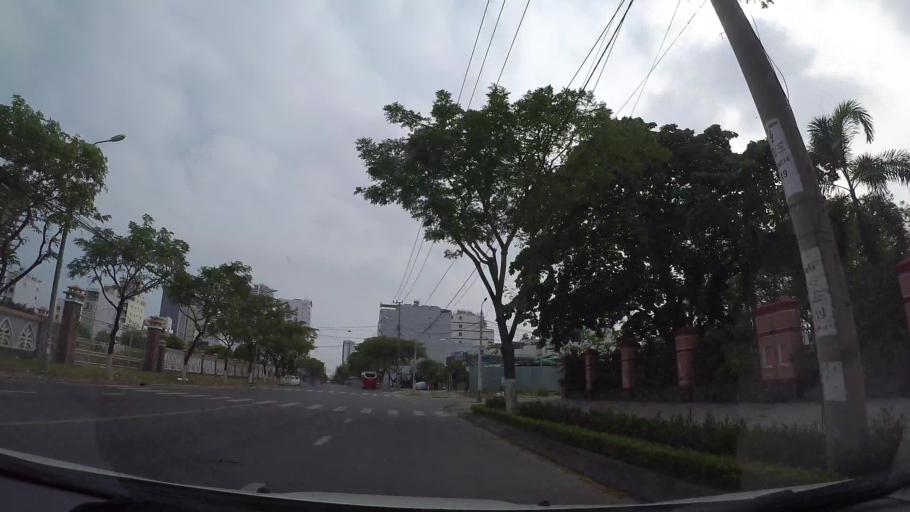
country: VN
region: Da Nang
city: Son Tra
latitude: 16.0785
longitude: 108.2428
